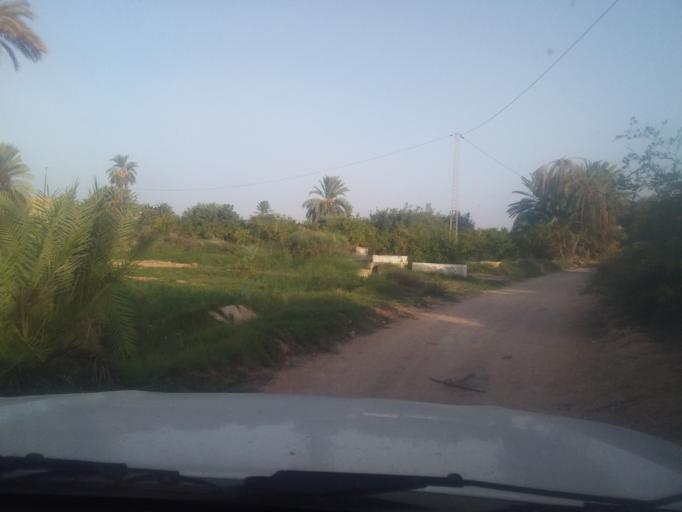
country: TN
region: Qabis
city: Gabes
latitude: 33.6311
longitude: 10.2945
